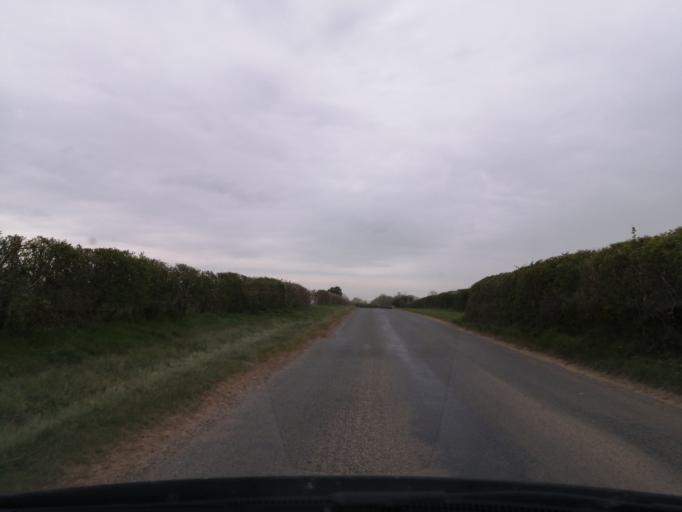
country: GB
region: England
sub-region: Peterborough
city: Wittering
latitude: 52.6056
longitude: -0.4621
